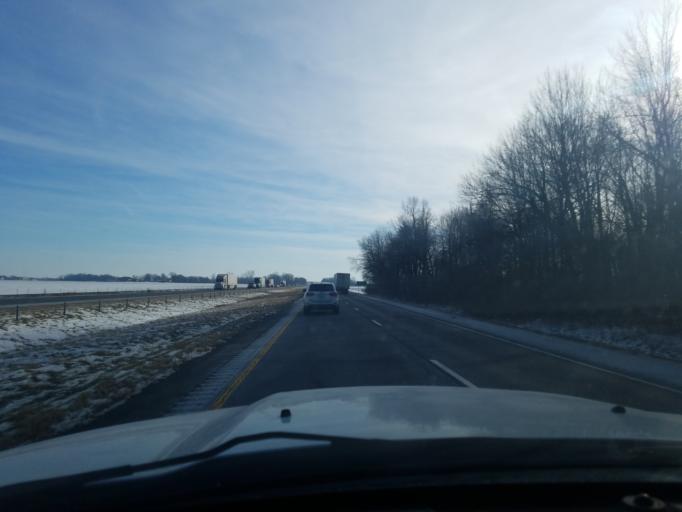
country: US
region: Indiana
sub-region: Madison County
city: Alexandria
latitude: 40.3006
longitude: -85.5585
